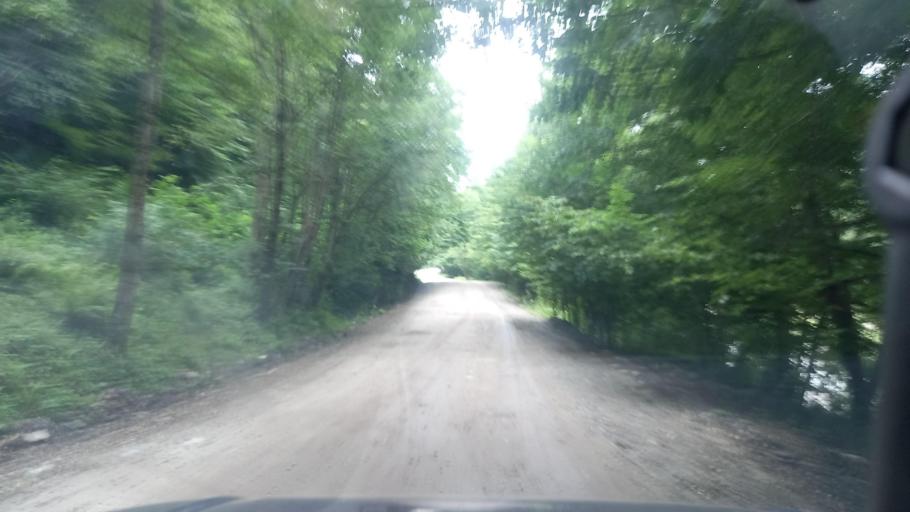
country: RU
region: Karachayevo-Cherkesiya
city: Kurdzhinovo
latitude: 43.8405
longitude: 40.9320
